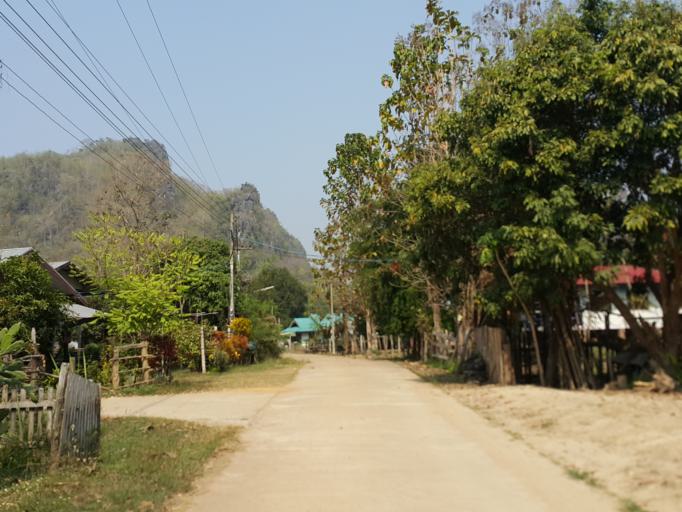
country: TH
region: Sukhothai
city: Thung Saliam
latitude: 17.3122
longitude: 99.5098
